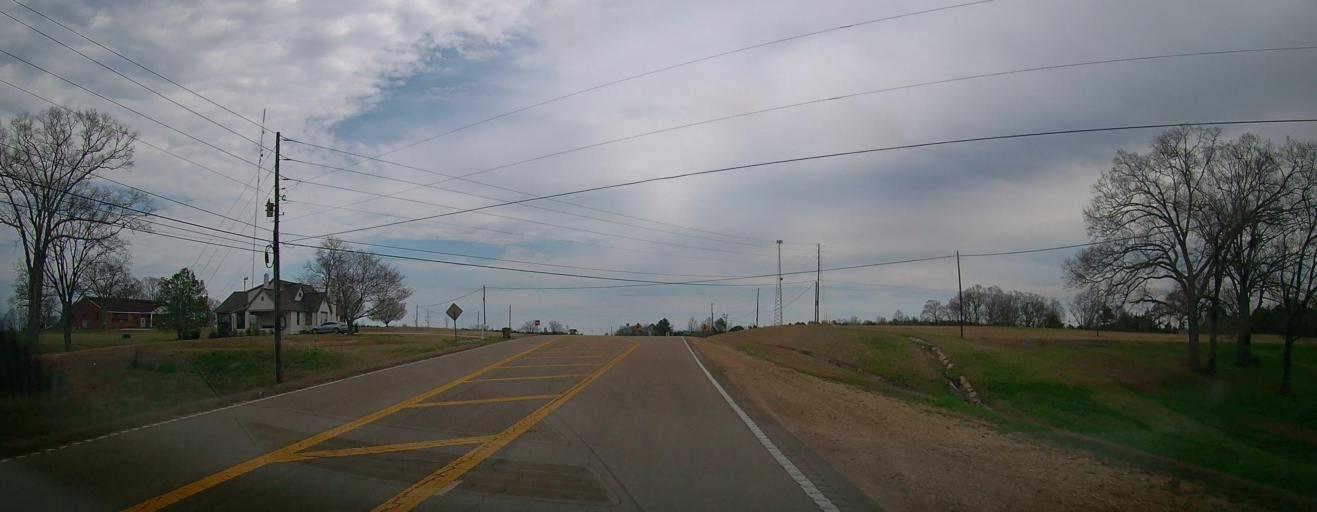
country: US
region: Mississippi
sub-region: Itawamba County
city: Fulton
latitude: 34.2680
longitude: -88.3342
